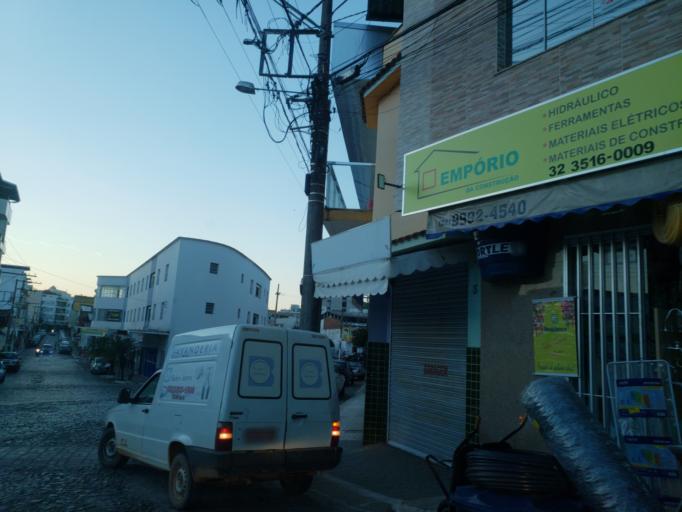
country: BR
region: Minas Gerais
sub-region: Sao Joao Nepomuceno
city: Sao Joao Nepomuceno
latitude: -21.5388
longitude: -43.0118
